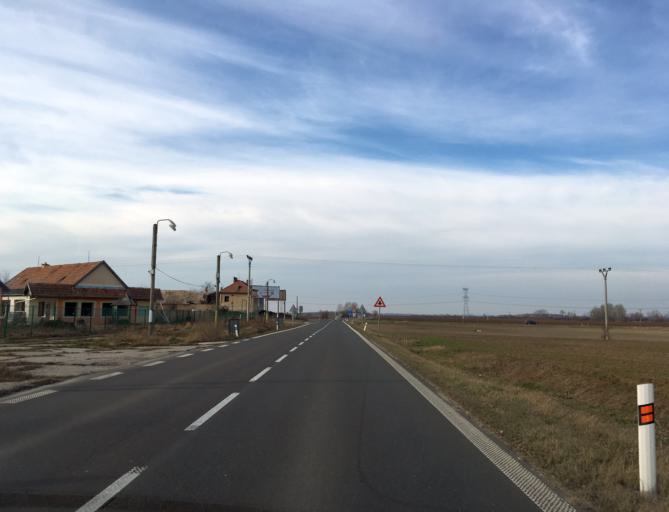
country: SK
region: Nitriansky
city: Surany
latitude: 48.0609
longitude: 18.1008
